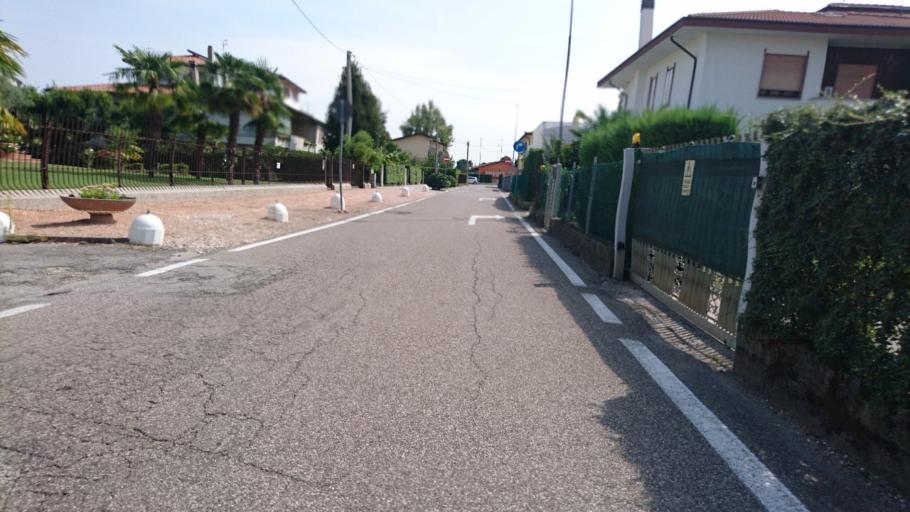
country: IT
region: Veneto
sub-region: Provincia di Padova
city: Mandriola-Sant'Agostino
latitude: 45.3605
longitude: 11.8690
